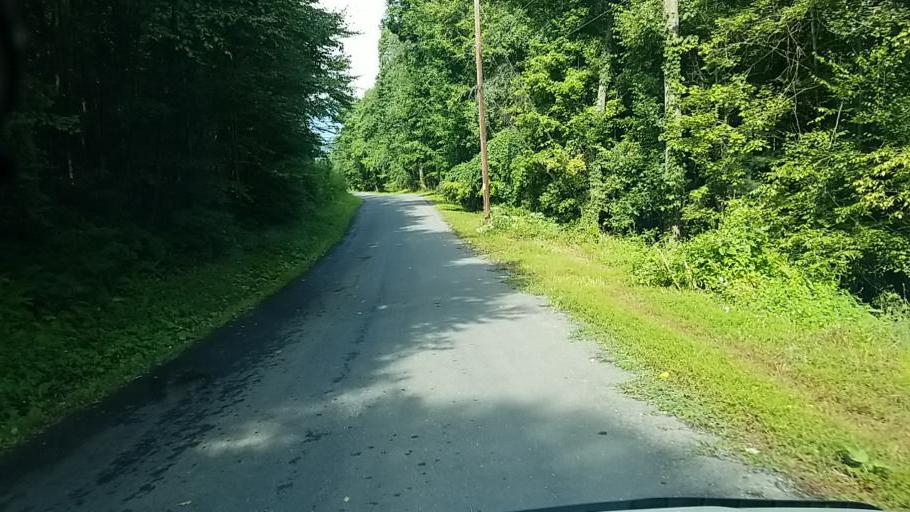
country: US
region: Pennsylvania
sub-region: Dauphin County
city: Millersburg
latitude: 40.5264
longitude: -76.9525
